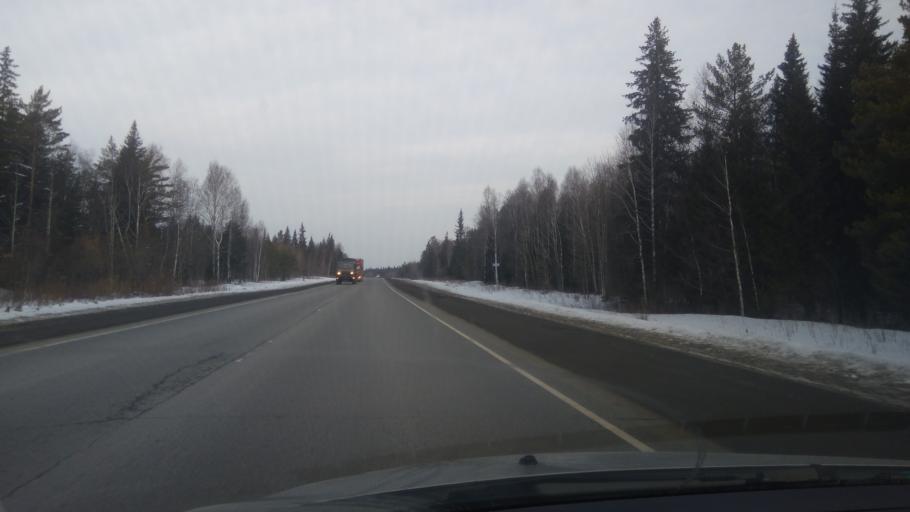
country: RU
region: Sverdlovsk
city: Atig
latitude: 56.8058
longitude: 59.3722
